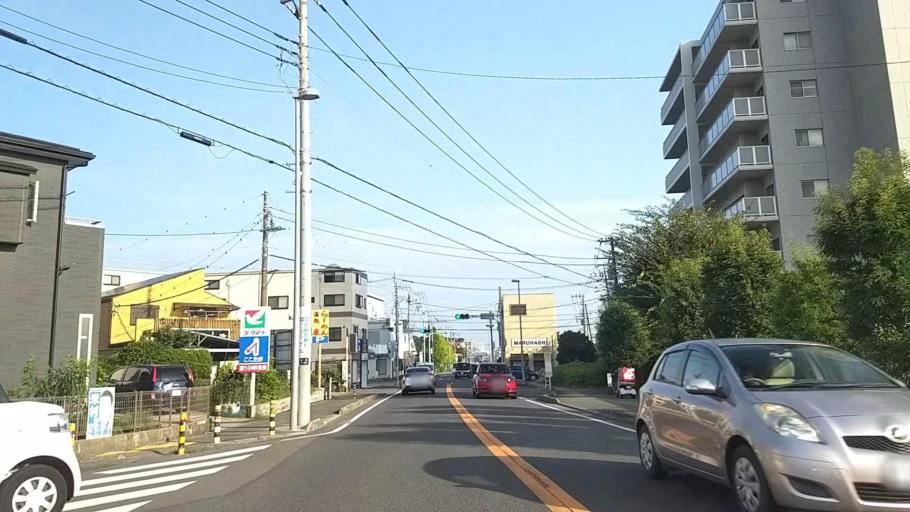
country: JP
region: Kanagawa
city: Hiratsuka
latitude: 35.3360
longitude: 139.3237
